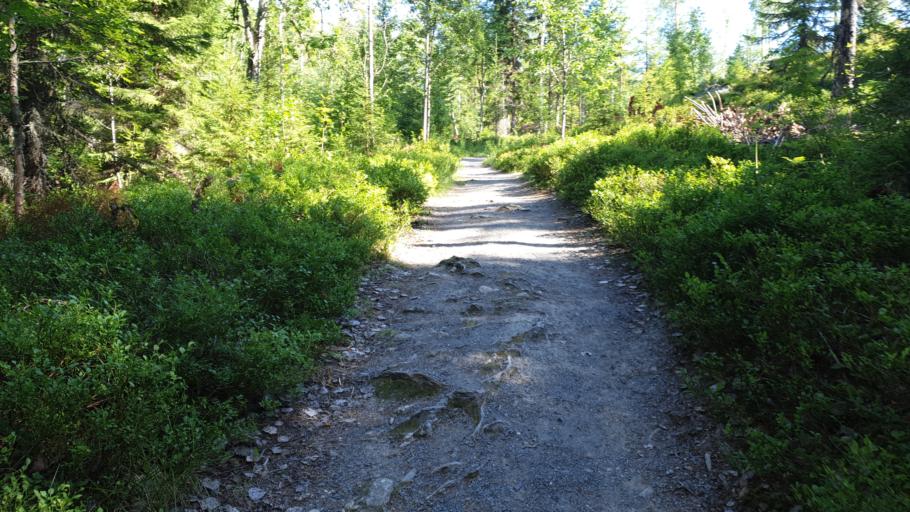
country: SE
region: Vaesternorrland
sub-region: OErnskoeldsviks Kommun
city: Husum
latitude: 63.4965
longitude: 18.9275
